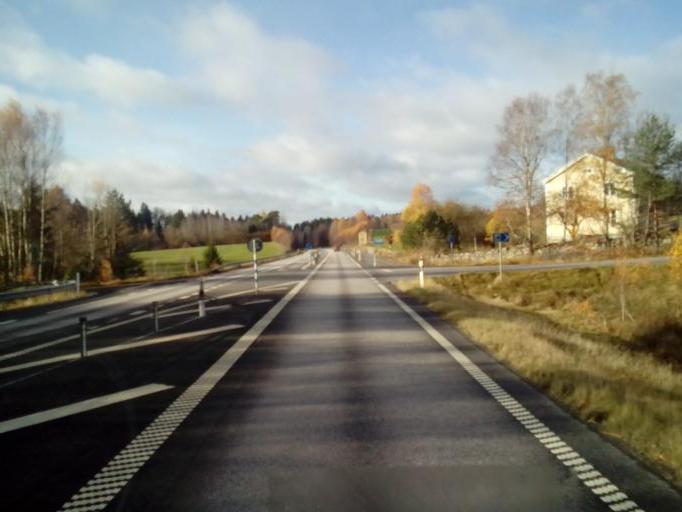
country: SE
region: Kalmar
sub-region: Vimmerby Kommun
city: Vimmerby
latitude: 57.6681
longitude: 15.9140
